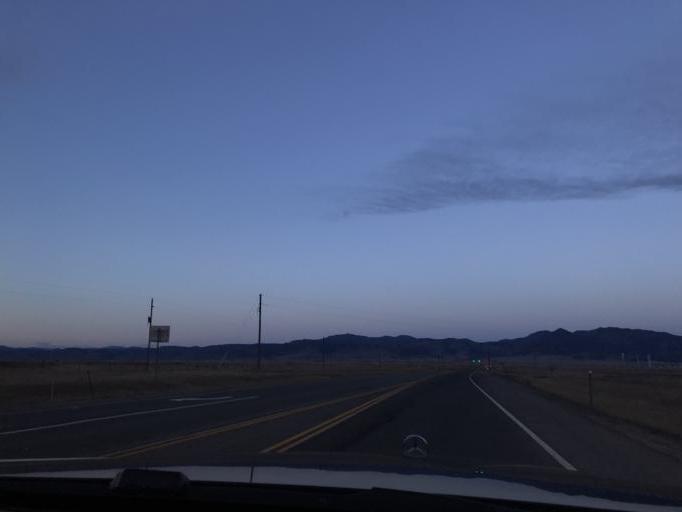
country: US
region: Colorado
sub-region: Boulder County
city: Superior
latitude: 39.9106
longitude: -105.1662
